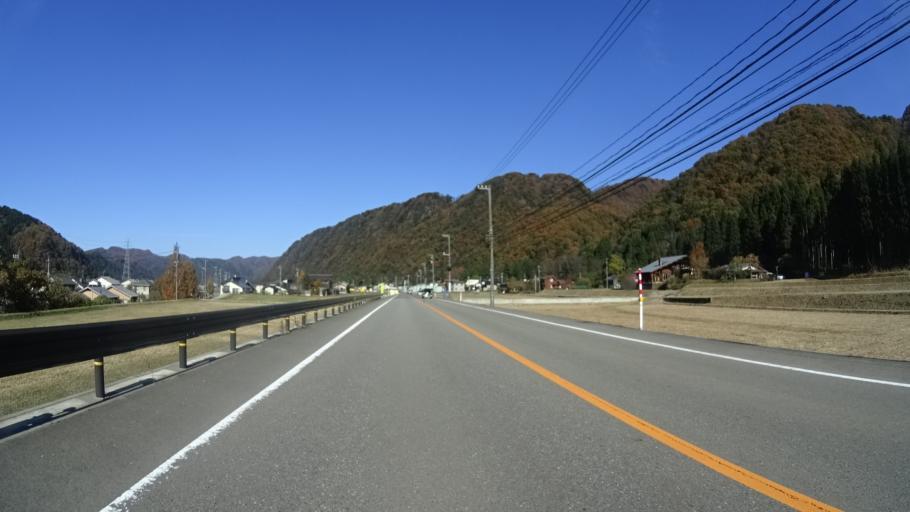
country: JP
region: Ishikawa
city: Tsurugi-asahimachi
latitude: 36.3556
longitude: 136.6240
